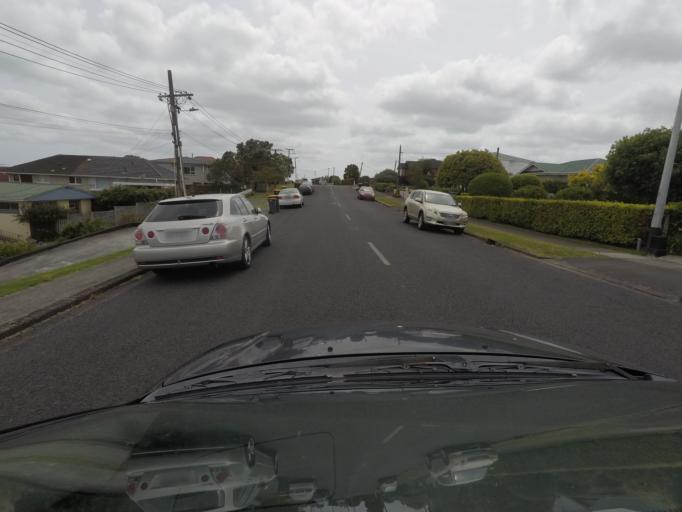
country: NZ
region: Auckland
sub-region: Auckland
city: Pakuranga
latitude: -36.8911
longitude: 174.9295
